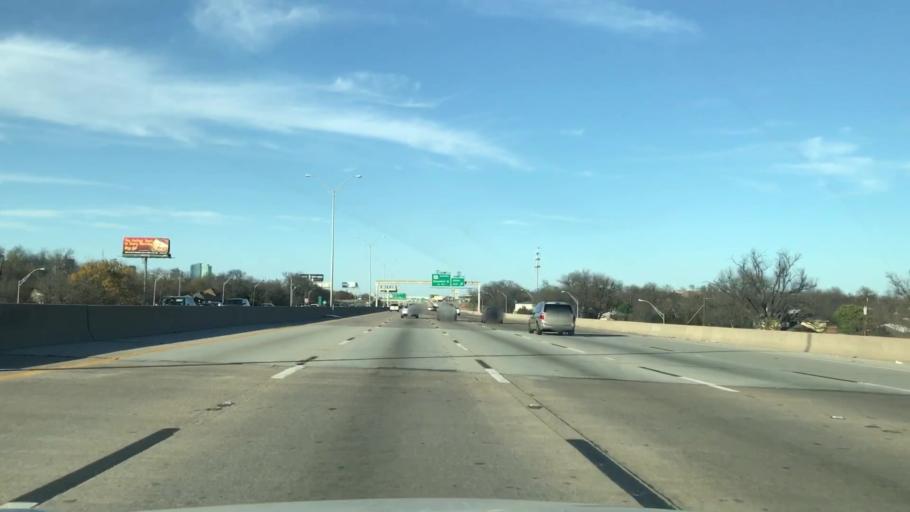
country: US
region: Texas
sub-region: Tarrant County
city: Fort Worth
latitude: 32.7188
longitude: -97.3205
